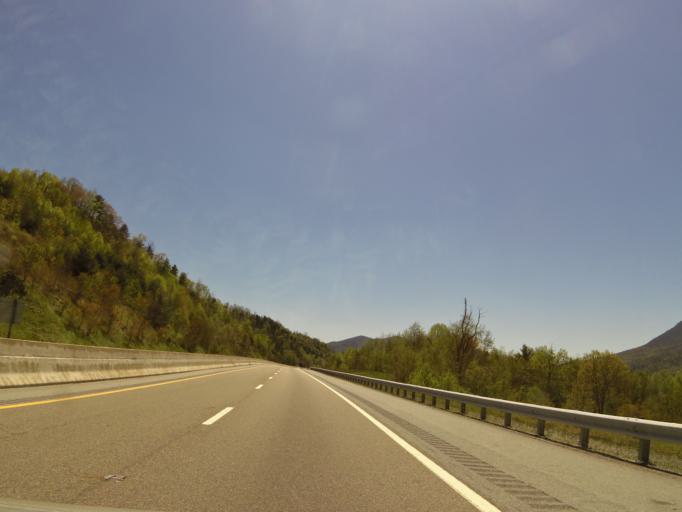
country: US
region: Tennessee
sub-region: Unicoi County
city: Banner Hill
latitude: 36.0429
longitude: -82.5280
